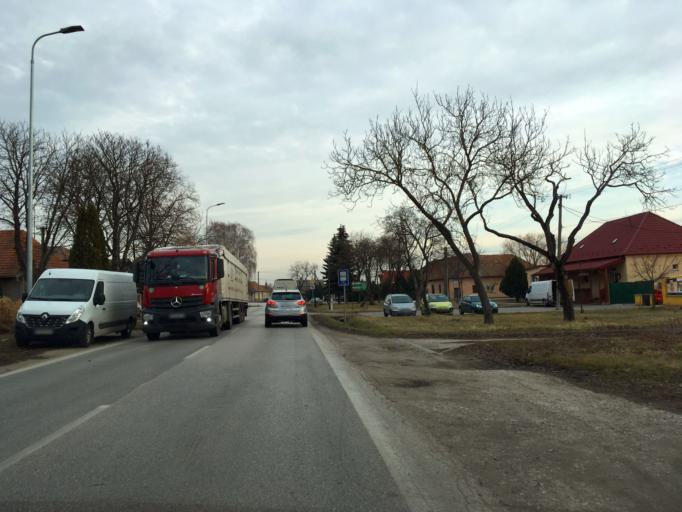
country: SK
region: Nitriansky
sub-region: Okres Nove Zamky
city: Nove Zamky
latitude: 47.9925
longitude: 18.2685
